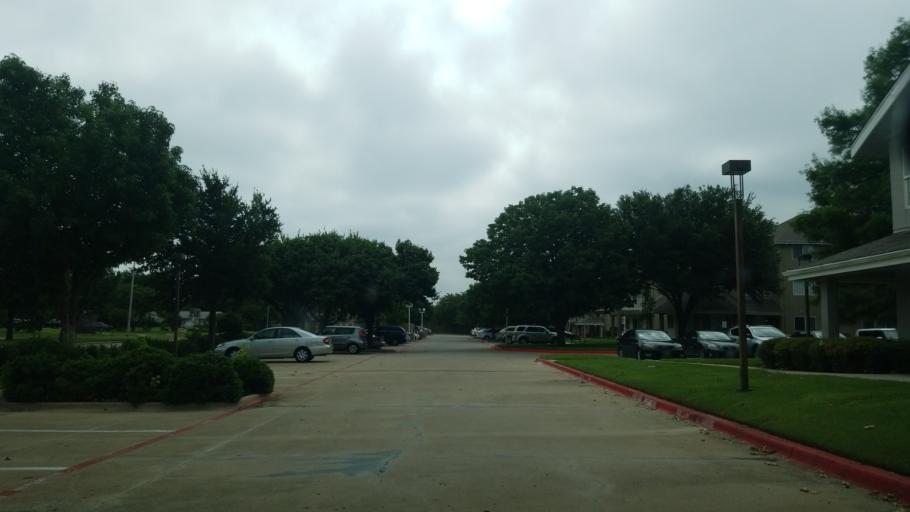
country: US
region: Texas
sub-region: Dallas County
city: Farmers Branch
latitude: 32.9094
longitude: -96.8666
